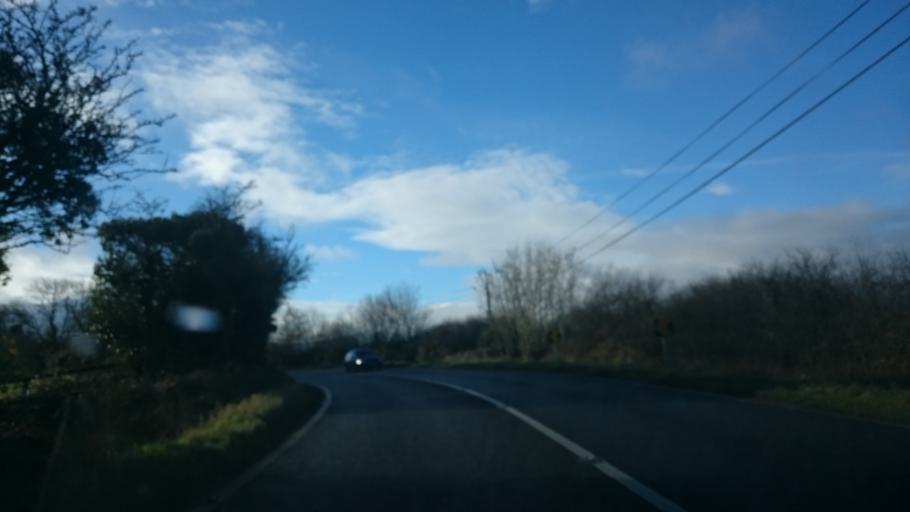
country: IE
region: Leinster
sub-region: Kilkenny
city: Kilkenny
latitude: 52.6152
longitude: -7.2874
